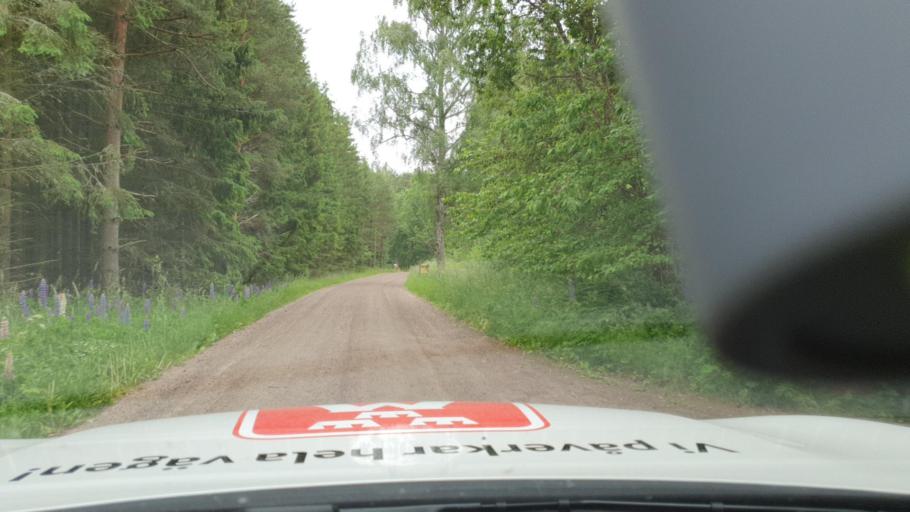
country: SE
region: Vaestra Goetaland
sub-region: Hjo Kommun
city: Hjo
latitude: 58.3903
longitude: 14.3431
